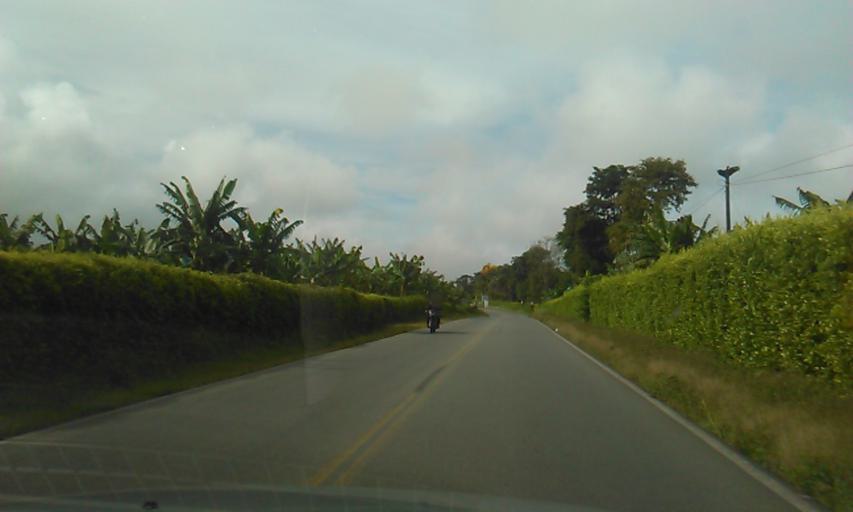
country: CO
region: Quindio
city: Cordoba
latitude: 4.4619
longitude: -75.7093
